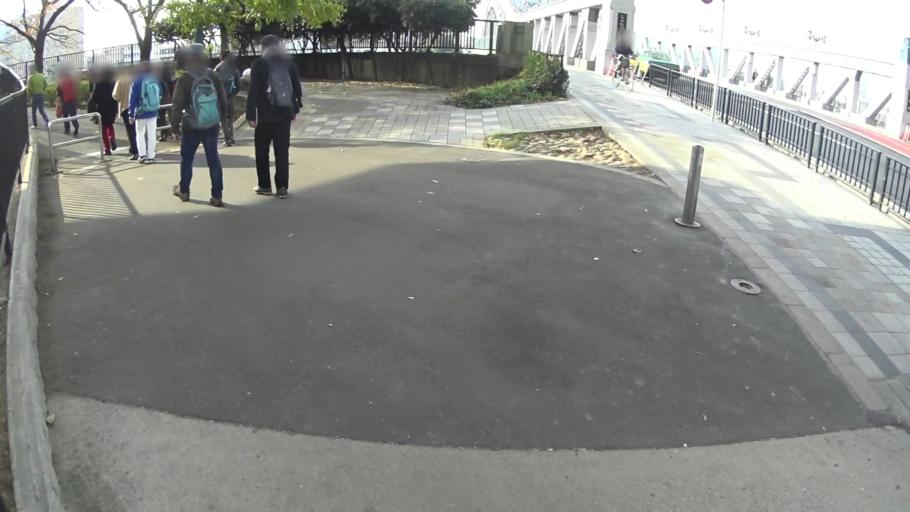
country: JP
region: Saitama
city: Soka
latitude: 35.7278
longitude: 139.8107
